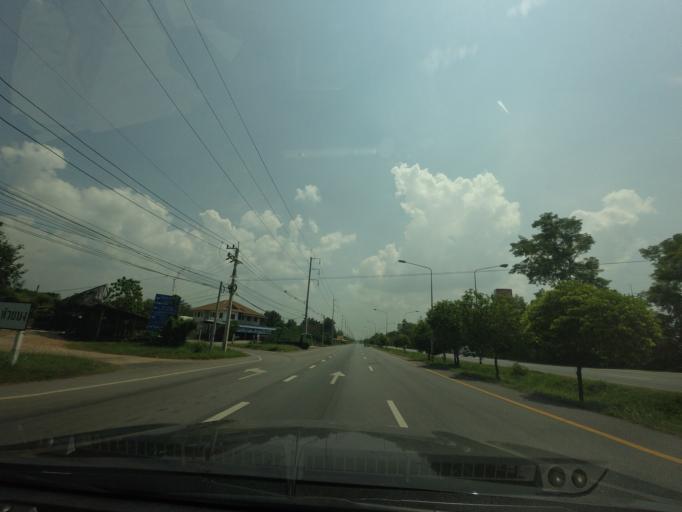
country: TH
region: Uttaradit
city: Uttaradit
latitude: 17.5795
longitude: 100.1444
